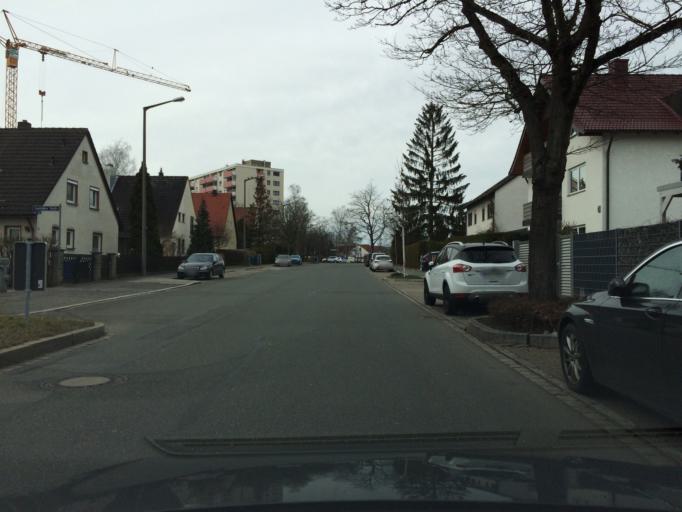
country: DE
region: Bavaria
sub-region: Regierungsbezirk Mittelfranken
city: Grossreuth bei Schweinau
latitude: 49.4239
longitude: 11.0269
